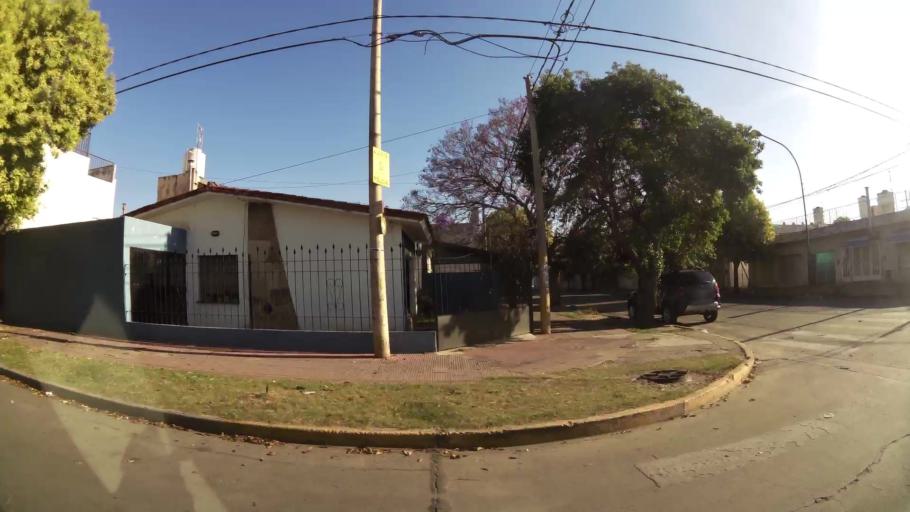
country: AR
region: Cordoba
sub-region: Departamento de Capital
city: Cordoba
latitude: -31.3806
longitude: -64.1810
